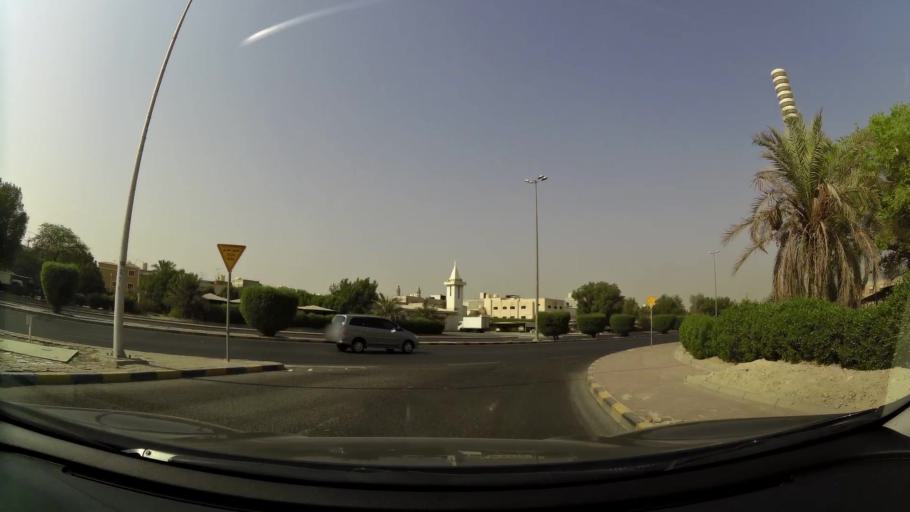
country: KW
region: Al Asimah
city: Ar Rabiyah
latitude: 29.2865
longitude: 47.8826
